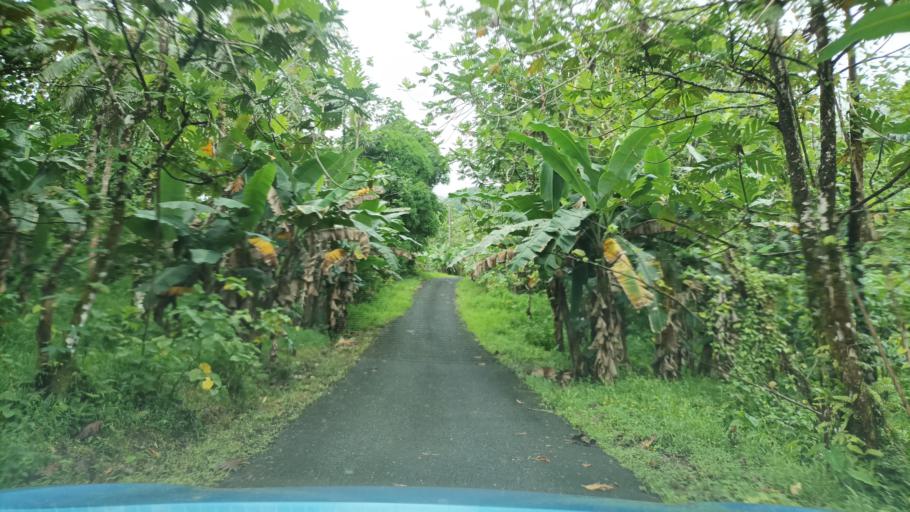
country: FM
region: Pohnpei
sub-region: Kolonia Municipality
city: Kolonia
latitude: 6.9193
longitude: 158.2733
